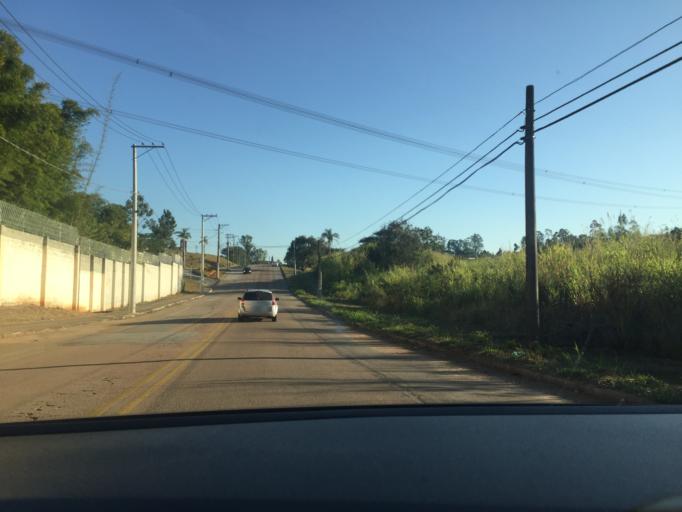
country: BR
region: Sao Paulo
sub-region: Louveira
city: Louveira
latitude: -23.1212
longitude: -46.9275
